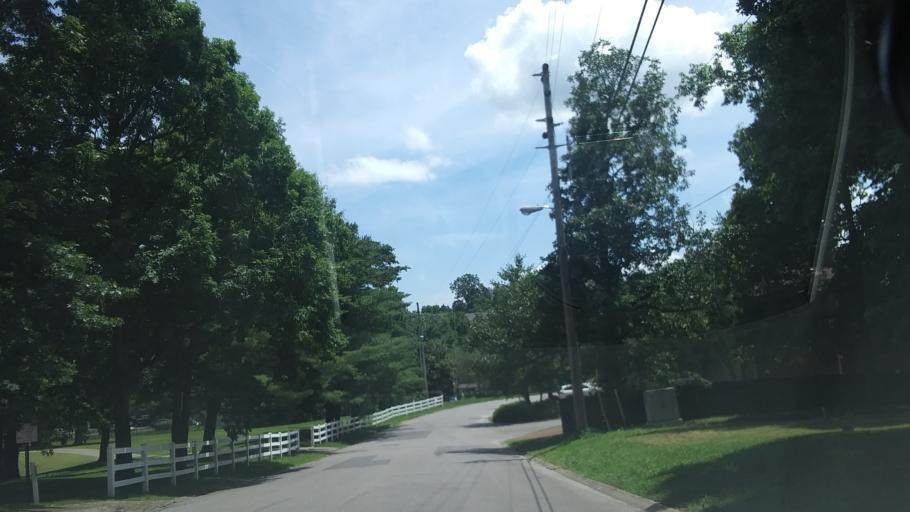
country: US
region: Tennessee
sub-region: Rutherford County
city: La Vergne
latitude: 36.0920
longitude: -86.6421
